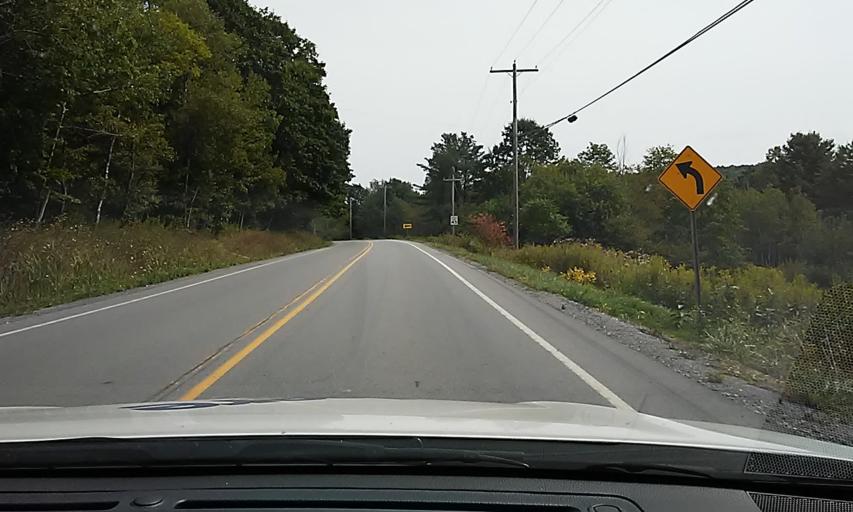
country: US
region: Pennsylvania
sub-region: Clearfield County
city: Treasure Lake
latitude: 41.2906
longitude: -78.6822
